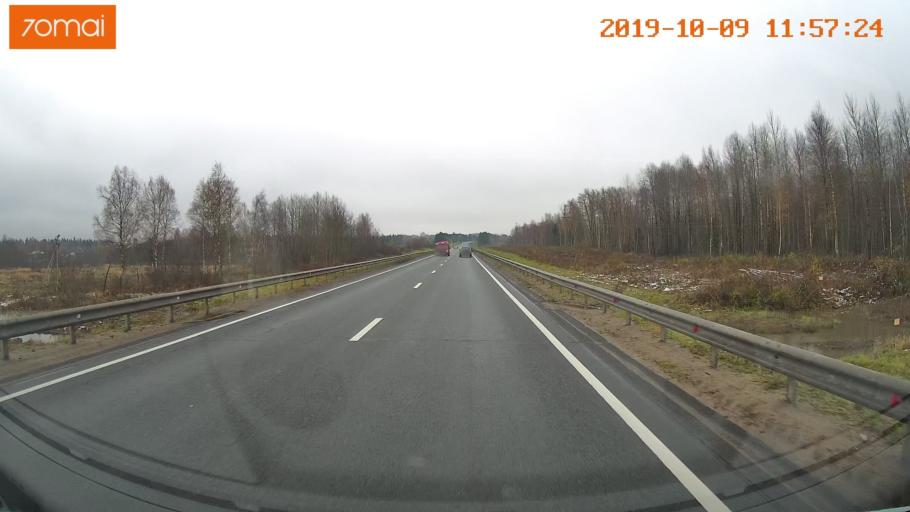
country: RU
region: Vologda
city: Gryazovets
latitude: 58.7326
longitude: 40.2924
